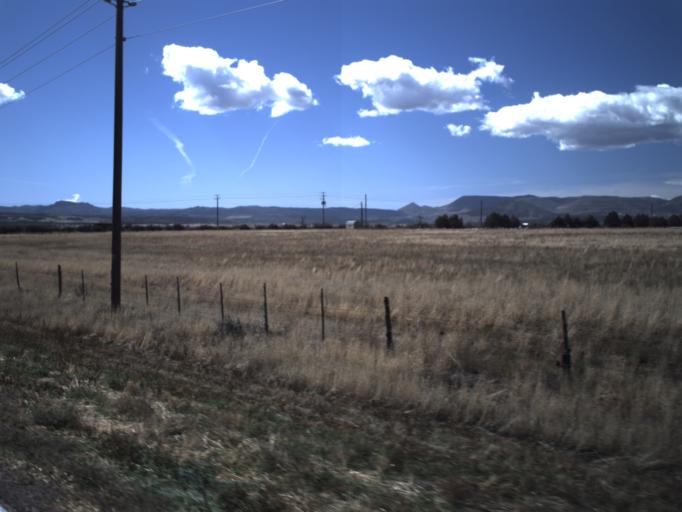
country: US
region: Utah
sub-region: Washington County
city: Enterprise
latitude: 37.6142
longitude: -113.6612
